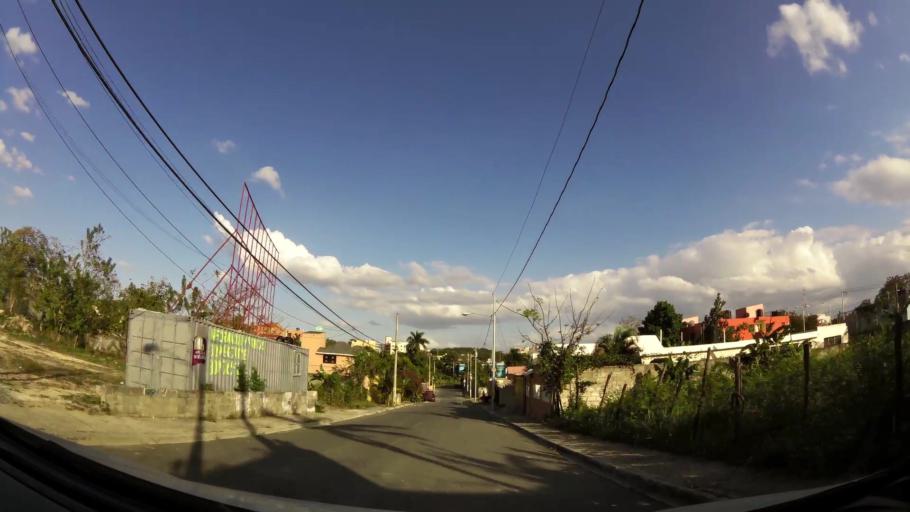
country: DO
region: Nacional
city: Ensanche Luperon
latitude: 18.5481
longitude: -69.9068
